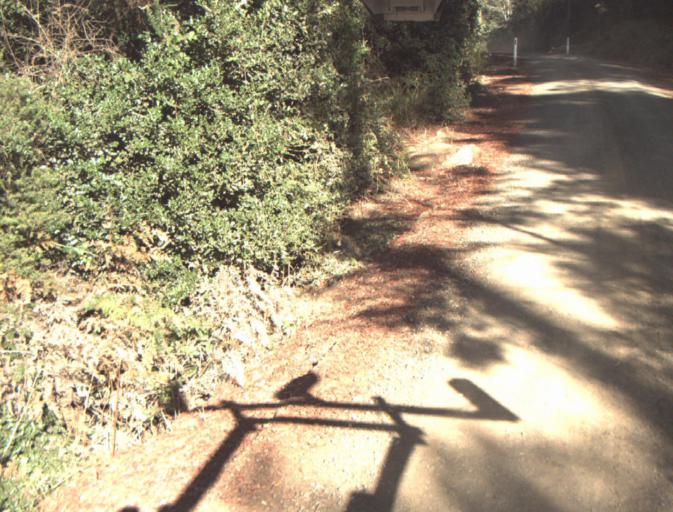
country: AU
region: Tasmania
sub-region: Launceston
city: Mayfield
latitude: -41.2903
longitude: 147.2010
